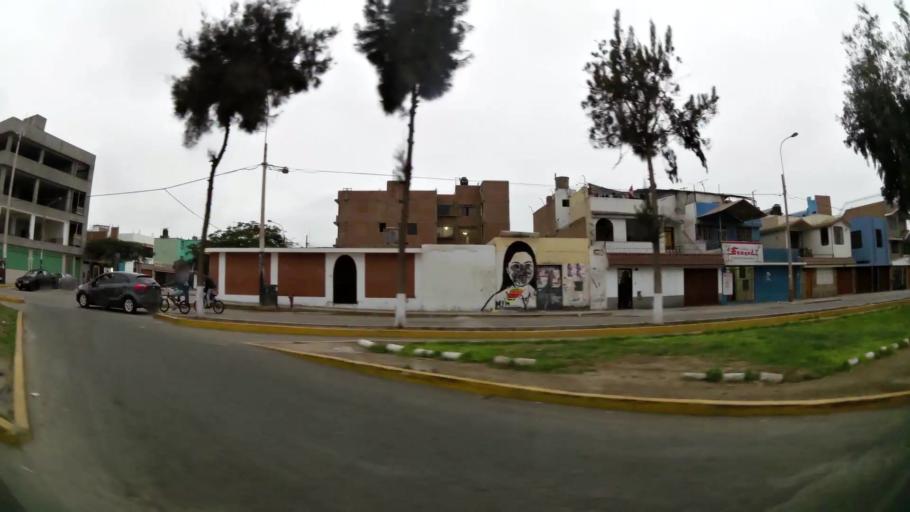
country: PE
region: Callao
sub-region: Callao
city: Callao
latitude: -12.0566
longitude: -77.1129
